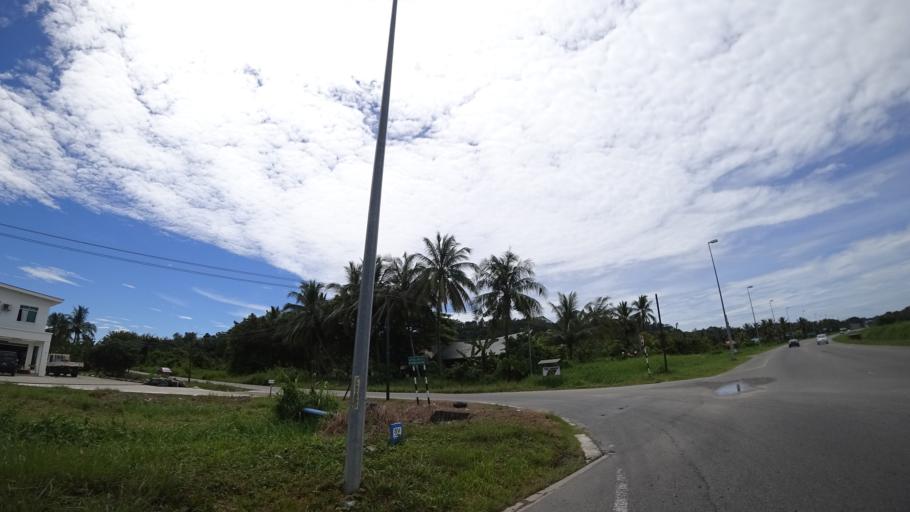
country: BN
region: Tutong
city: Tutong
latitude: 4.7882
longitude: 114.8239
